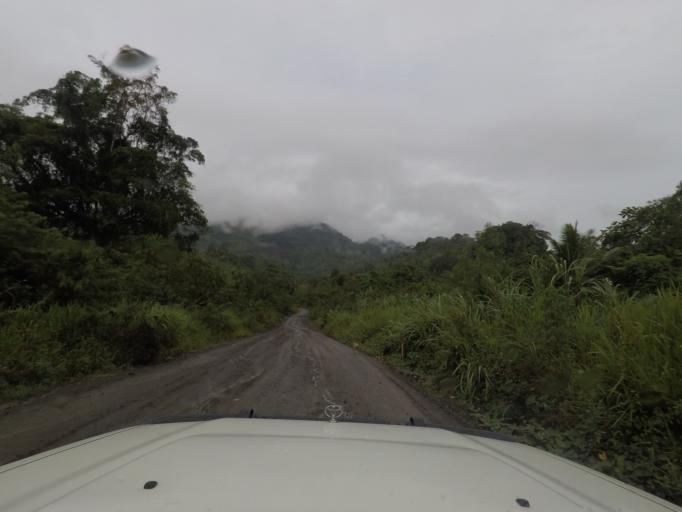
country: PG
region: Madang
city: Madang
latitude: -5.4829
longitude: 145.4848
